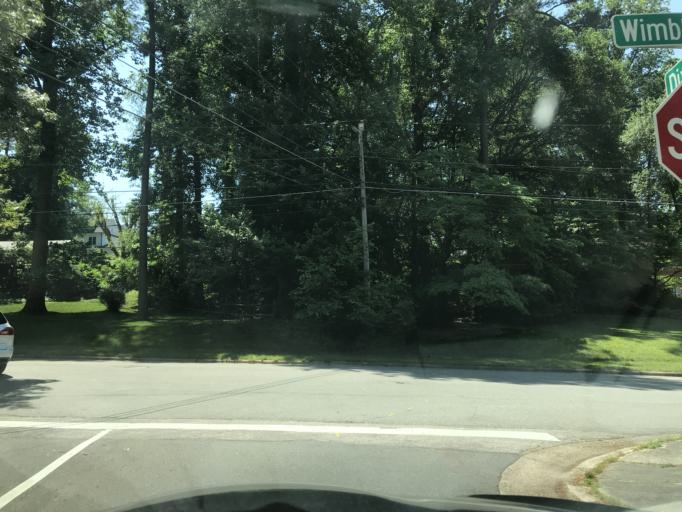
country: US
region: North Carolina
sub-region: Wake County
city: West Raleigh
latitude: 35.8531
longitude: -78.6506
